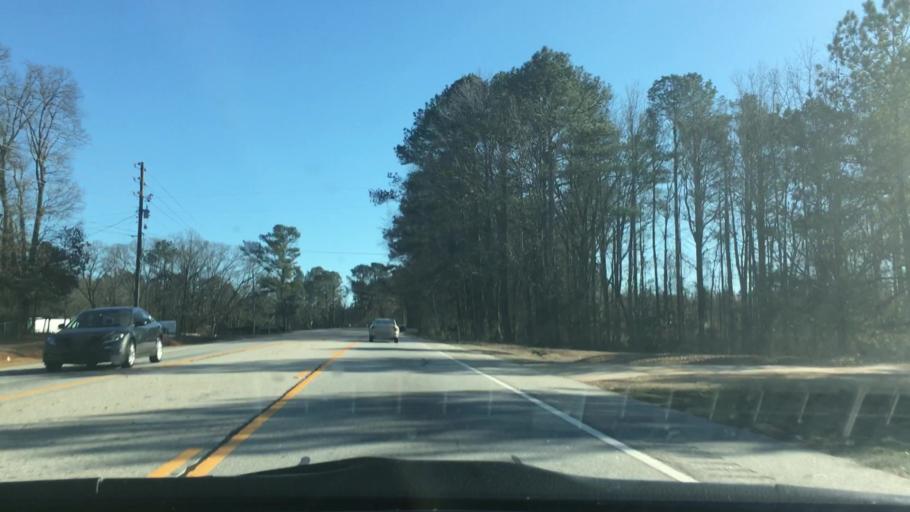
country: US
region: Georgia
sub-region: Henry County
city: McDonough
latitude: 33.5213
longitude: -84.1392
